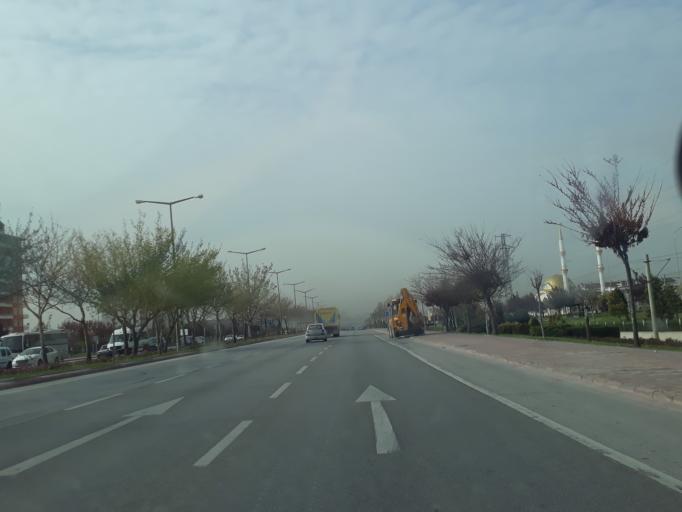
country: TR
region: Konya
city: Asagipinarbasi
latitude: 37.9923
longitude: 32.5185
